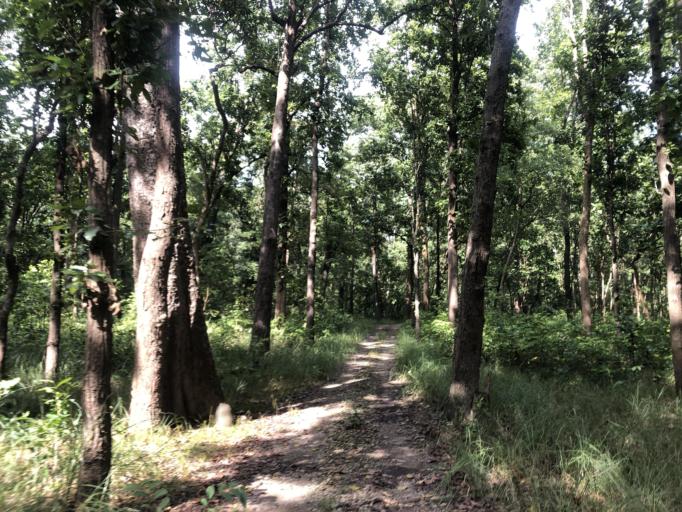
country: NP
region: Far Western
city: Tikapur
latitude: 28.5485
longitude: 81.2877
